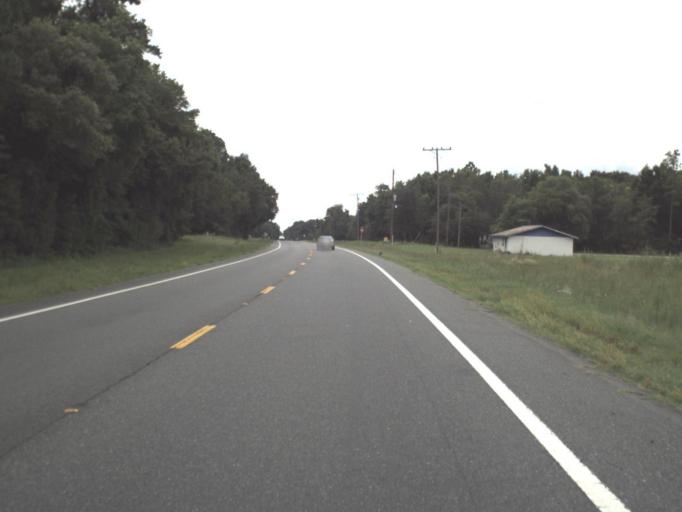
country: US
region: Florida
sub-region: Levy County
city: Williston Highlands
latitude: 29.2206
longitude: -82.4409
